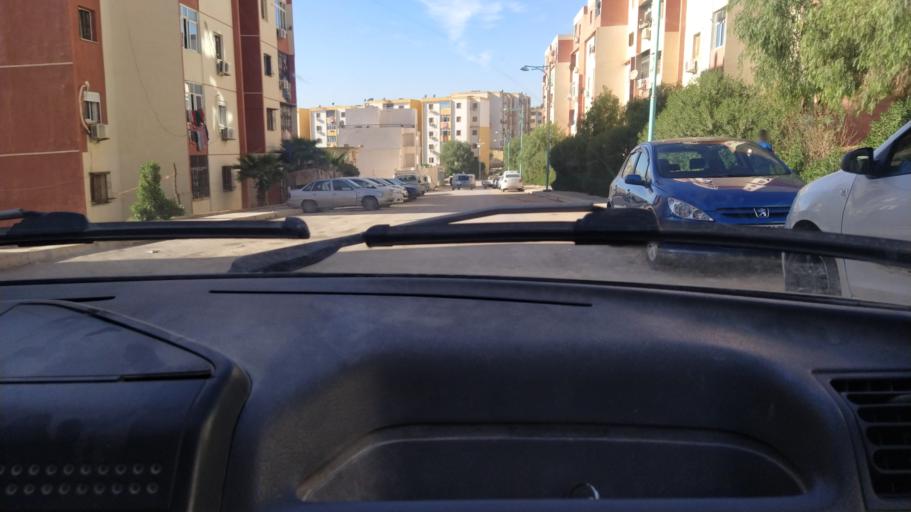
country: DZ
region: Constantine
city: Ain Smara
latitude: 36.2504
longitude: 6.5563
